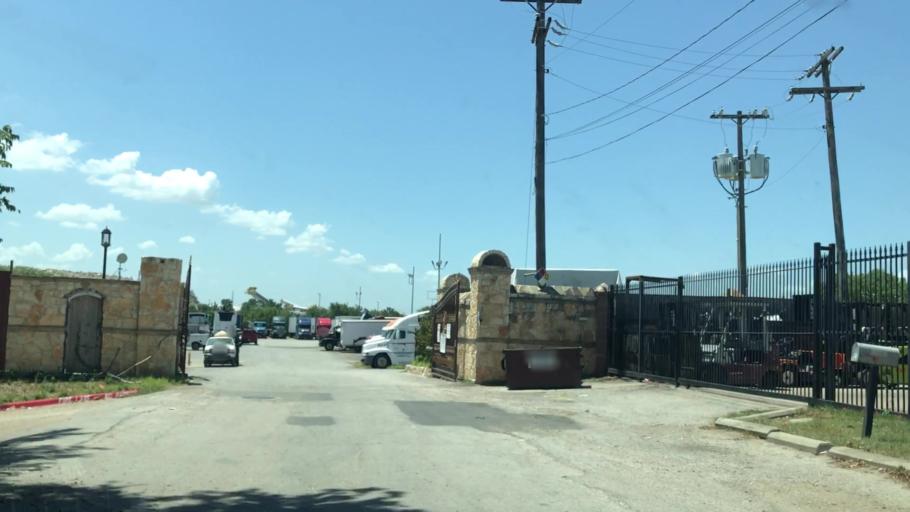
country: US
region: Texas
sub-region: Dallas County
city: Farmers Branch
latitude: 32.8924
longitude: -96.9112
